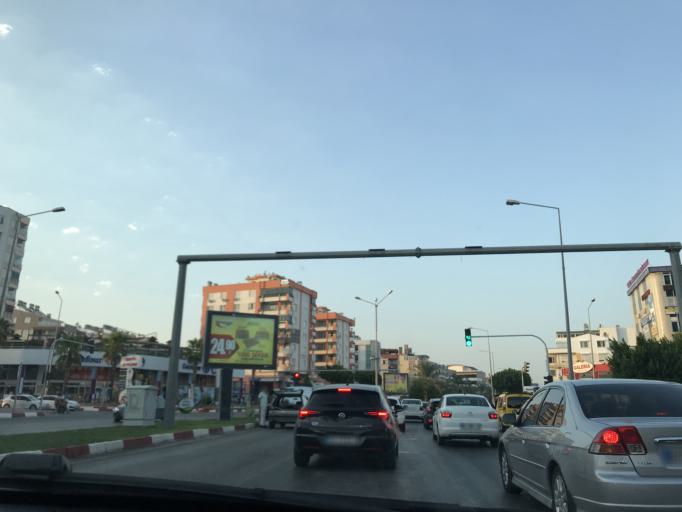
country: TR
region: Antalya
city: Antalya
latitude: 36.8742
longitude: 30.6426
